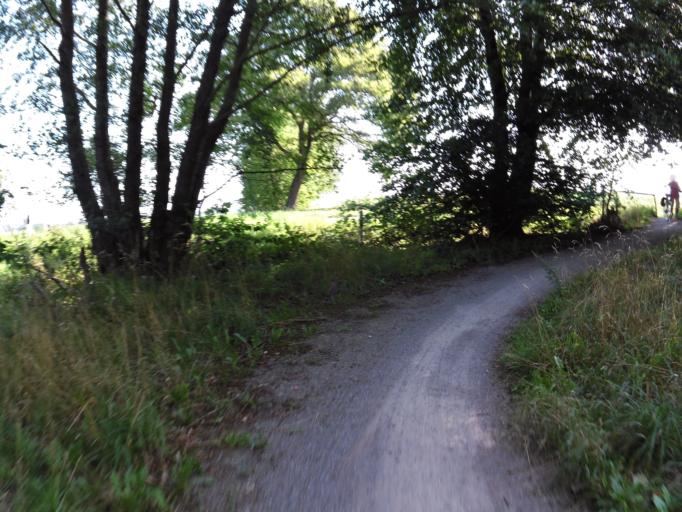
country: DE
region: North Rhine-Westphalia
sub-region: Regierungsbezirk Munster
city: Vreden
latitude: 51.9938
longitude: 6.8279
